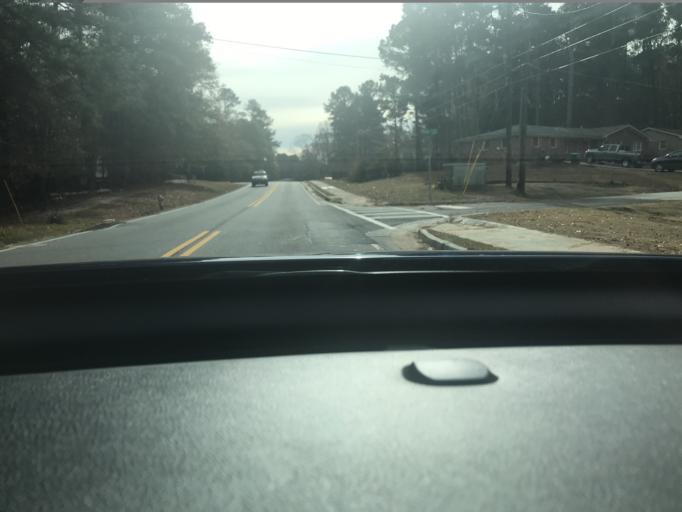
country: US
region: Georgia
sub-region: Gwinnett County
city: Mountain Park
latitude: 33.8359
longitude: -84.1292
